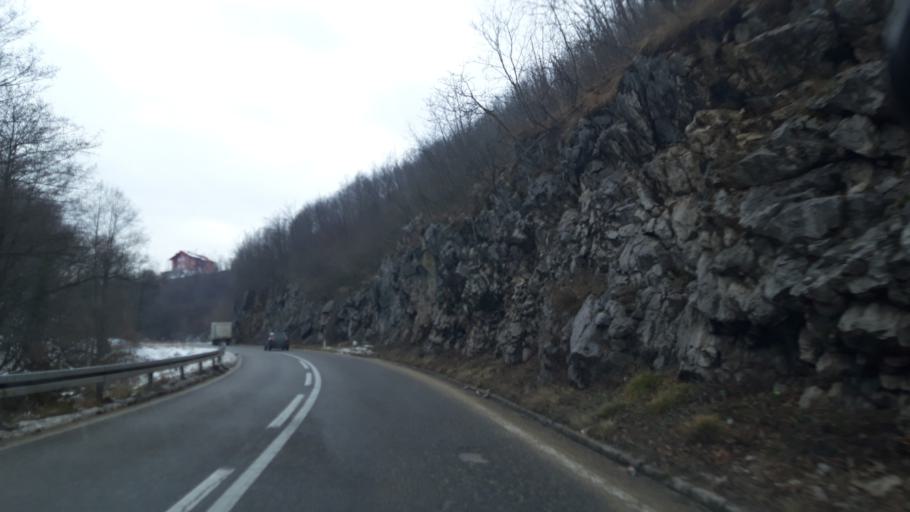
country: BA
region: Republika Srpska
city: Vlasenica
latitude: 44.1837
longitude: 18.9742
